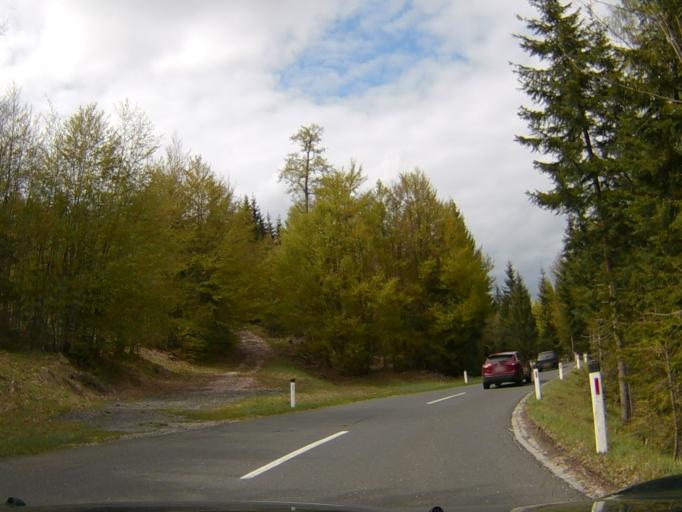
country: AT
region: Carinthia
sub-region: Politischer Bezirk Villach Land
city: Arnoldstein
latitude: 46.5937
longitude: 13.7688
